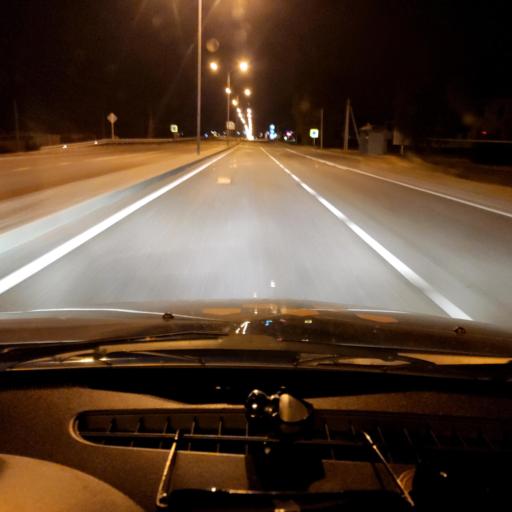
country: RU
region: Belgorod
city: Gubkin
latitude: 51.2628
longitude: 37.5423
